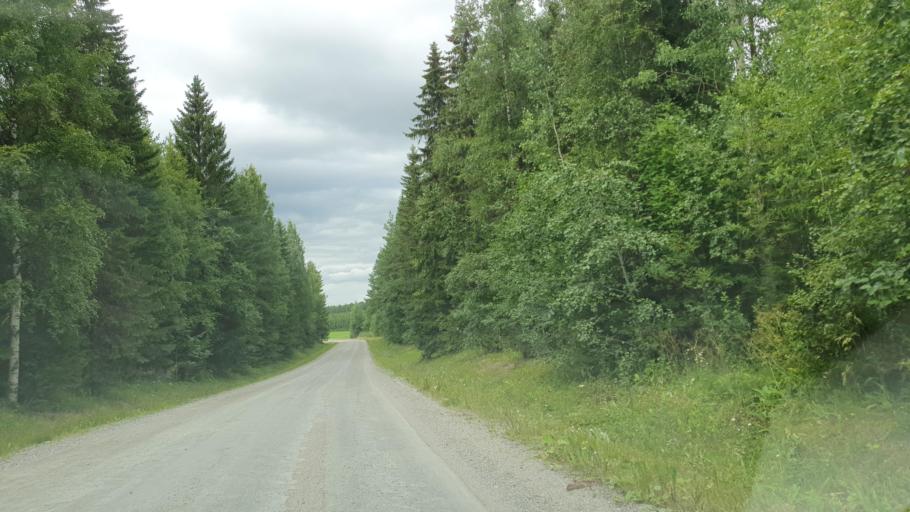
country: FI
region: Northern Savo
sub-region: Ylae-Savo
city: Iisalmi
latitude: 63.5386
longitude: 27.0741
